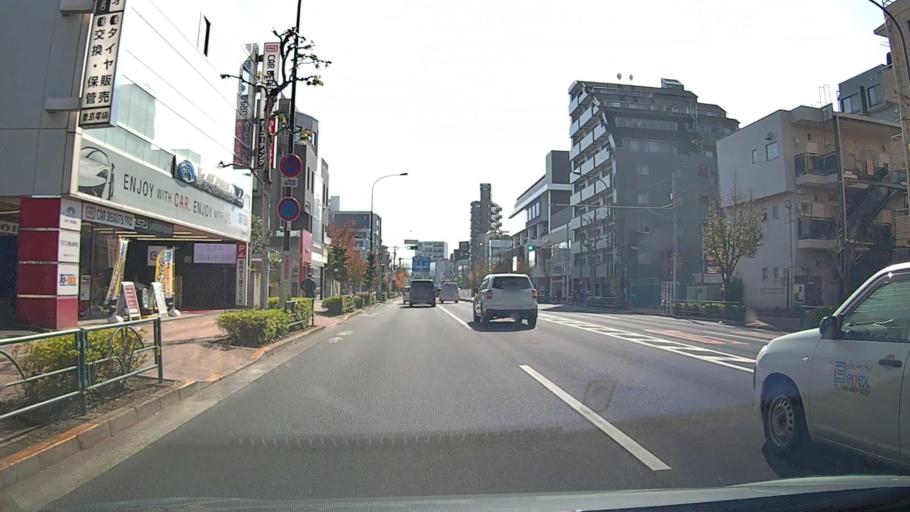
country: JP
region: Tokyo
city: Tokyo
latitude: 35.7254
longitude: 139.6825
